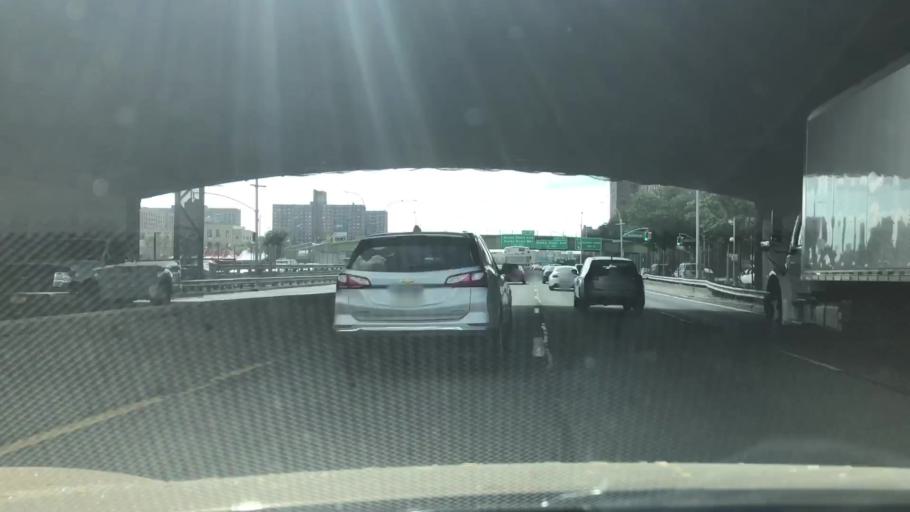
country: US
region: New York
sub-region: Bronx
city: The Bronx
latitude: 40.8240
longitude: -73.8730
